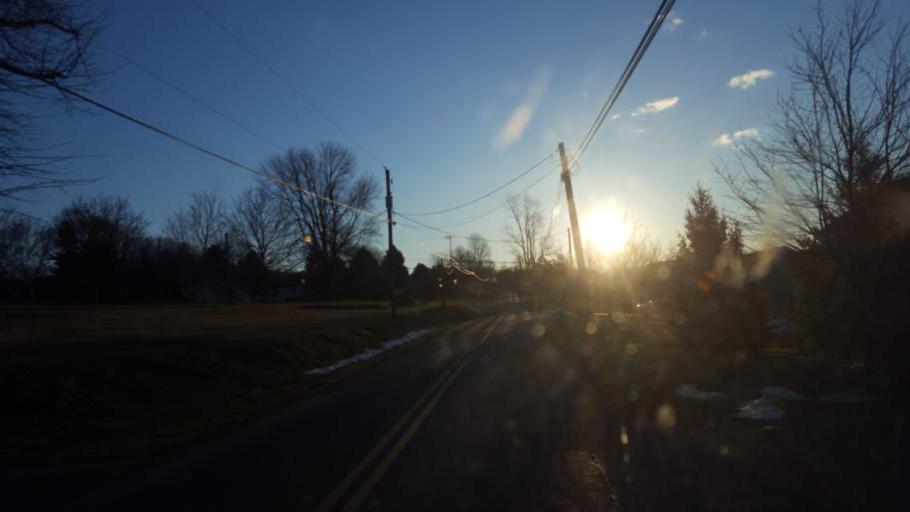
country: US
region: Pennsylvania
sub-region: Lancaster County
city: New Holland
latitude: 40.0745
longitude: -76.0756
